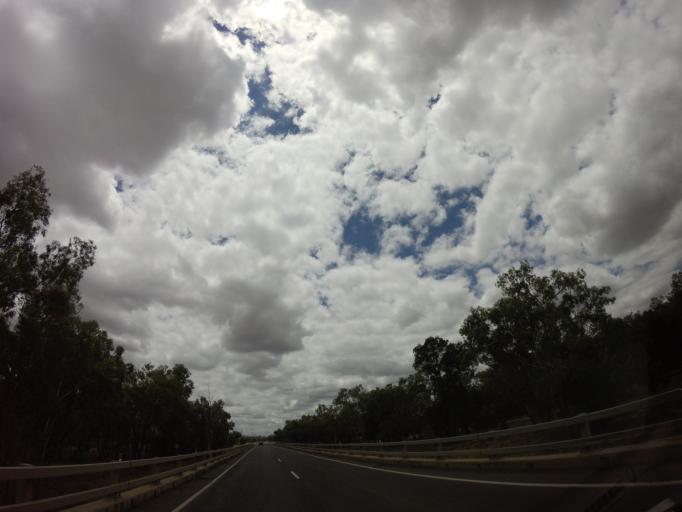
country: AU
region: Queensland
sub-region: Goondiwindi
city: Goondiwindi
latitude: -28.3978
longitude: 150.3118
